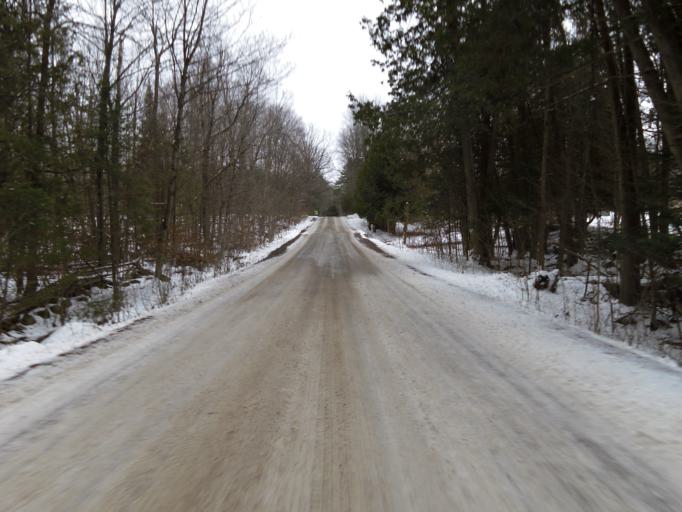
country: CA
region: Ontario
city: Carleton Place
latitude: 45.1480
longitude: -76.2533
